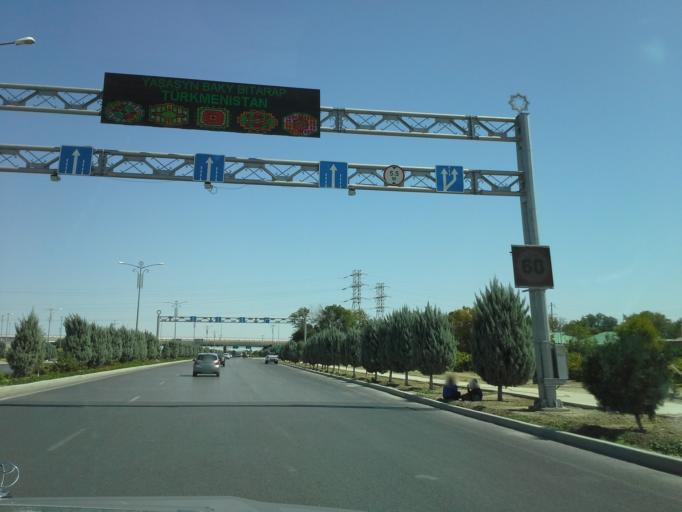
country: TM
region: Ahal
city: Annau
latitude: 37.9143
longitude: 58.4803
